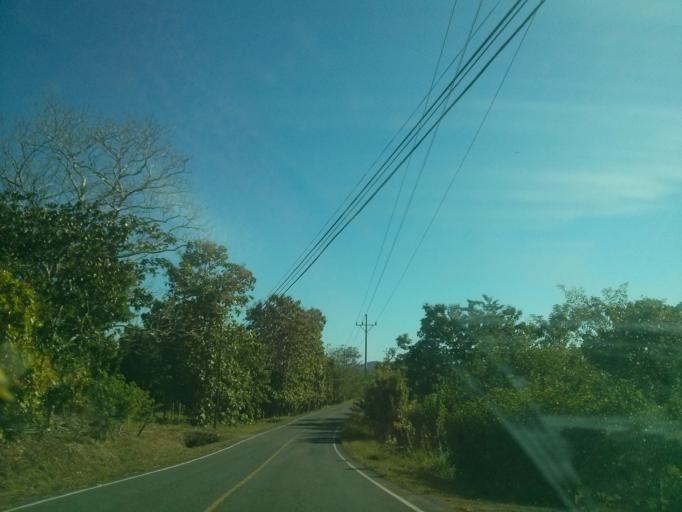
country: CR
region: Puntarenas
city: Paquera
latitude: 9.6987
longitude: -85.0737
